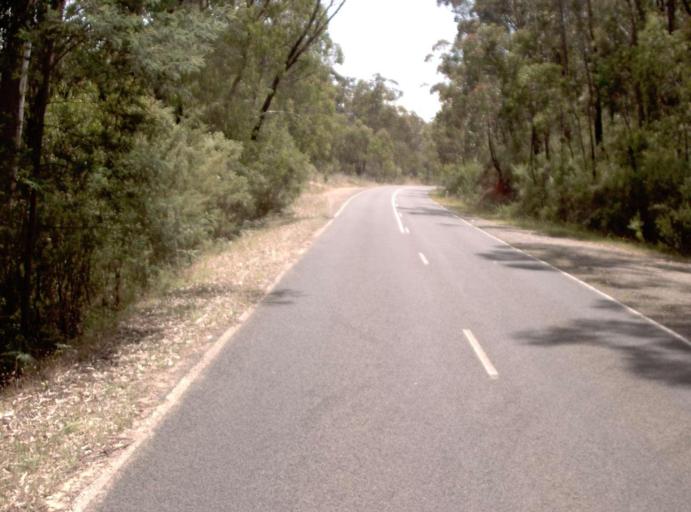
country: AU
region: Victoria
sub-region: Latrobe
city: Moe
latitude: -38.0280
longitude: 146.3518
